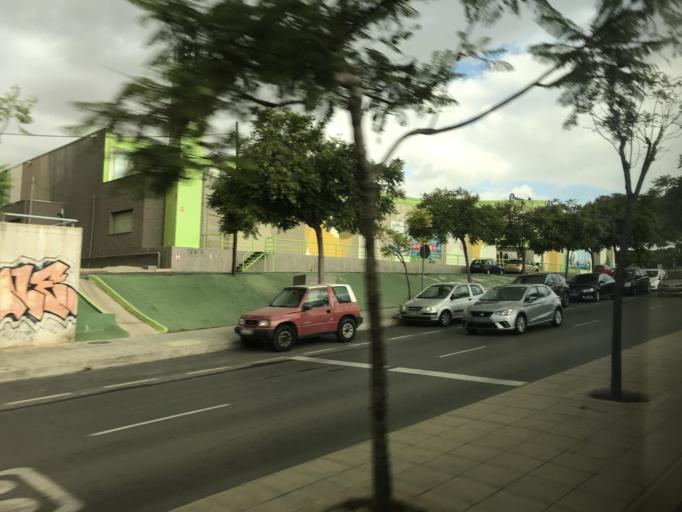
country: ES
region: Valencia
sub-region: Provincia de Alicante
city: Santa Pola
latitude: 38.1982
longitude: -0.5619
